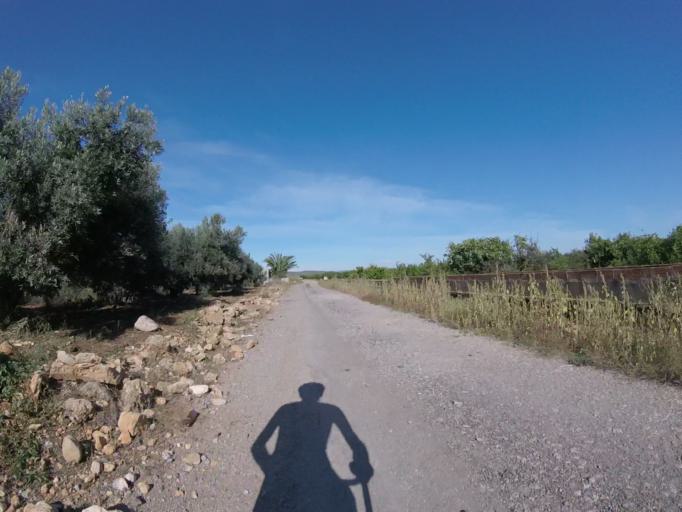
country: ES
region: Valencia
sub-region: Provincia de Castello
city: Torreblanca
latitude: 40.2084
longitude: 0.2349
